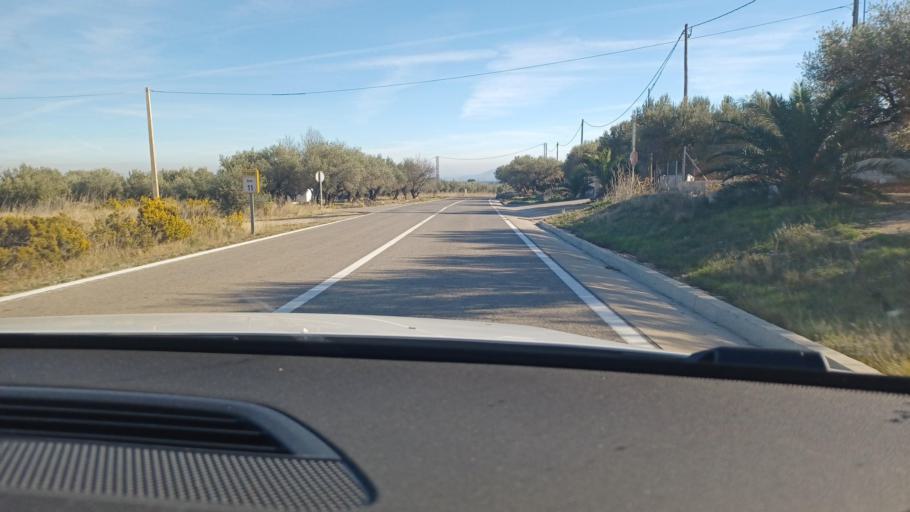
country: ES
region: Catalonia
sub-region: Provincia de Tarragona
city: Mas de Barberans
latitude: 40.7302
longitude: 0.3772
